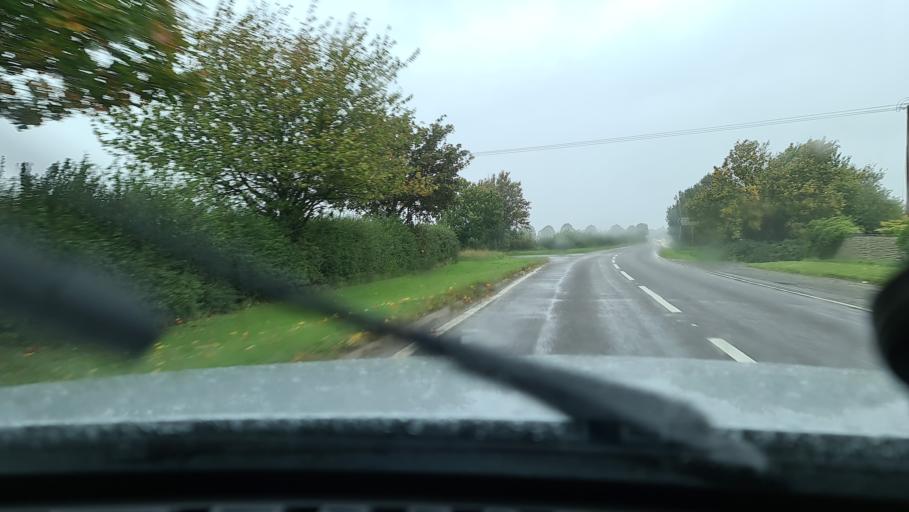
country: GB
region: England
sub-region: Oxfordshire
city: Deddington
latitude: 51.9337
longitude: -1.3258
